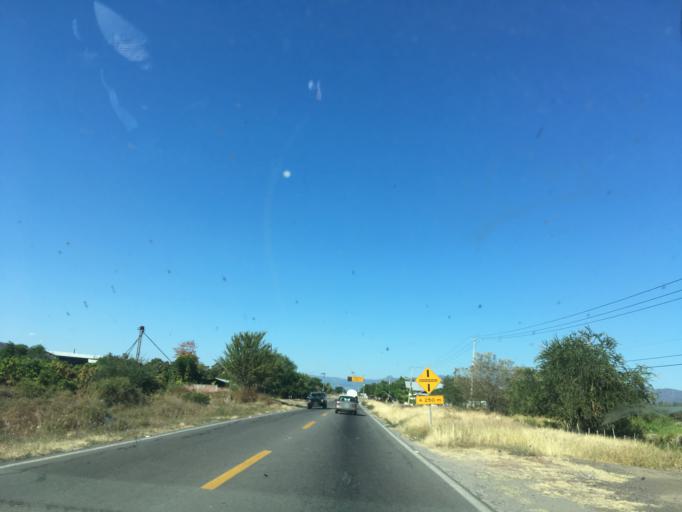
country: MX
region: Michoacan
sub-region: Gabriel Zamora
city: Lombardia
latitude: 19.0937
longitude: -102.0581
